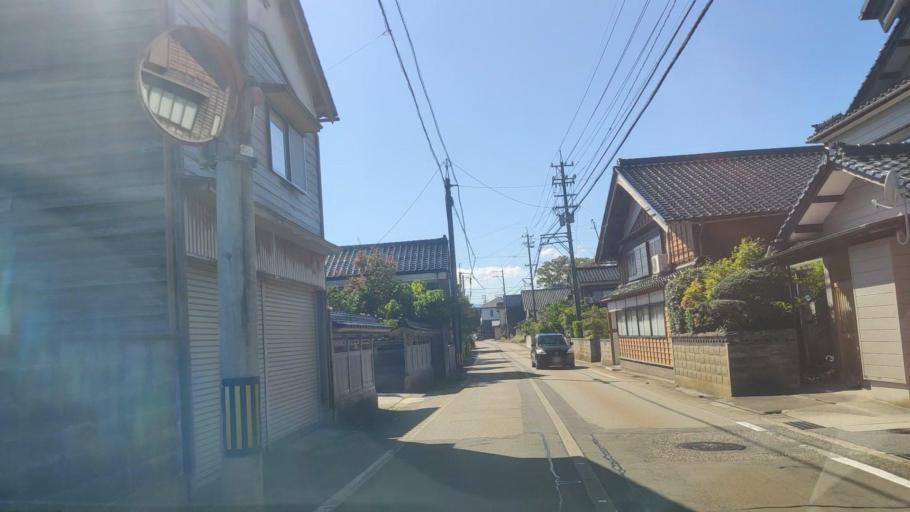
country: JP
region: Ishikawa
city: Nanao
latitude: 37.4419
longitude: 137.2801
